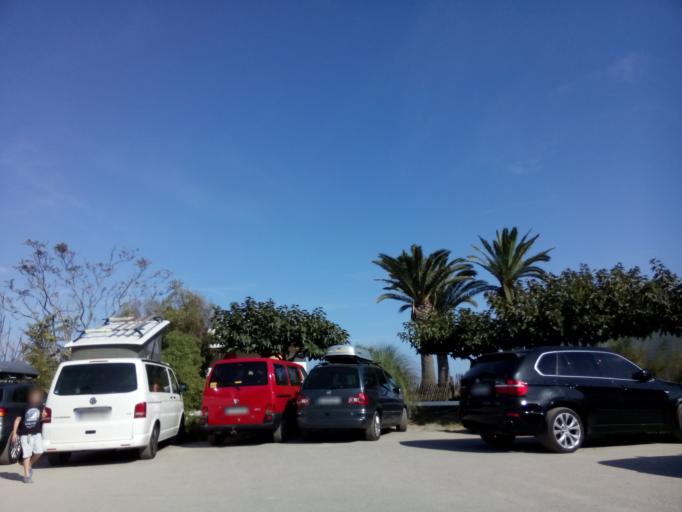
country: FR
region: Corsica
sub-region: Departement de la Haute-Corse
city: Aleria
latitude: 42.1075
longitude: 9.5494
